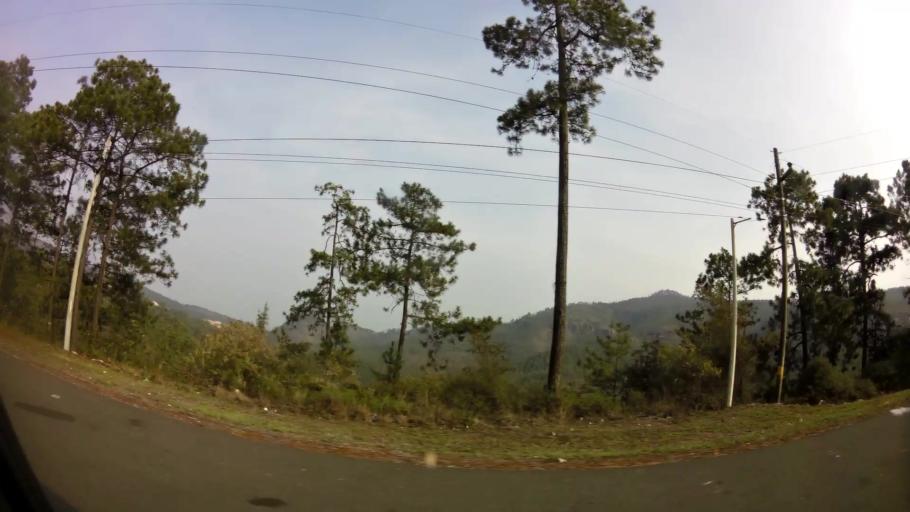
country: HN
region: Francisco Morazan
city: Zambrano
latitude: 14.2854
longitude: -87.4607
